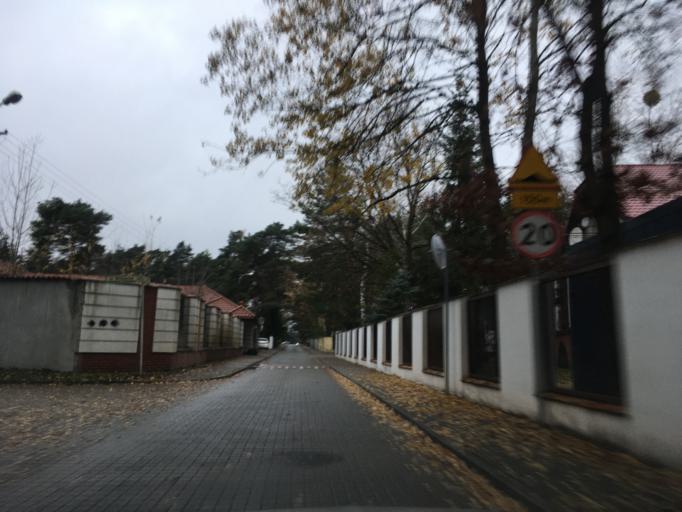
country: PL
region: Masovian Voivodeship
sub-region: Powiat piaseczynski
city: Lesznowola
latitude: 52.0901
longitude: 20.8960
